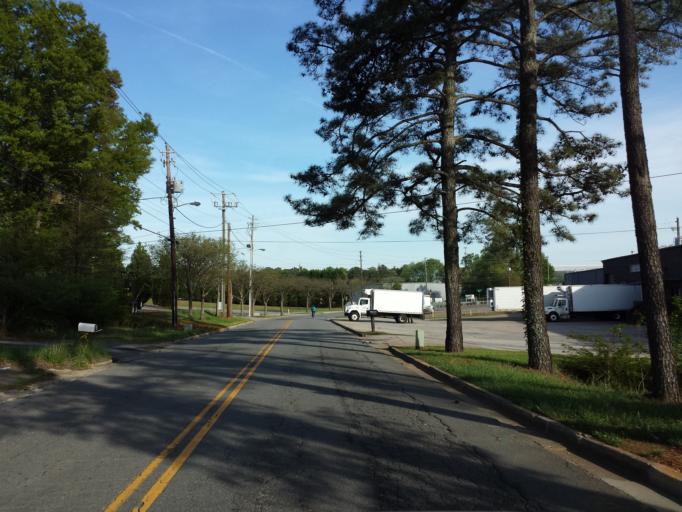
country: US
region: Georgia
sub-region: Cobb County
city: Marietta
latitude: 33.9754
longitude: -84.5392
